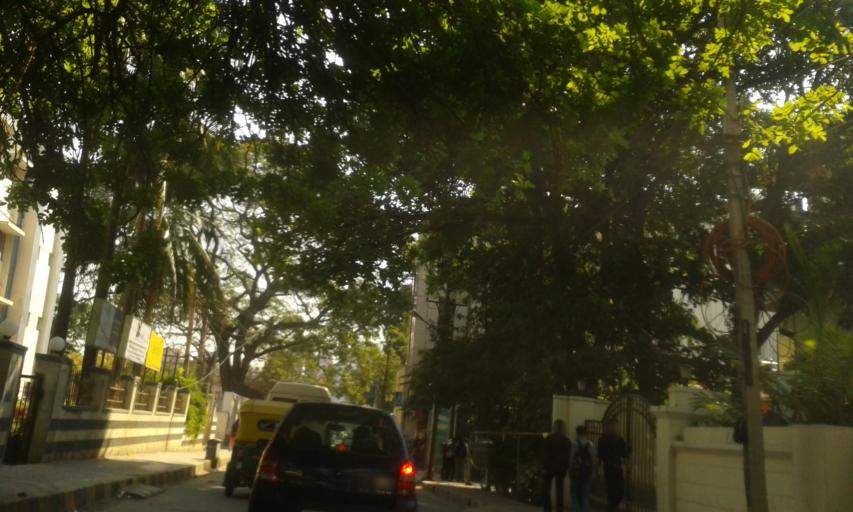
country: IN
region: Karnataka
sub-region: Bangalore Urban
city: Bangalore
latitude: 12.9710
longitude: 77.6082
